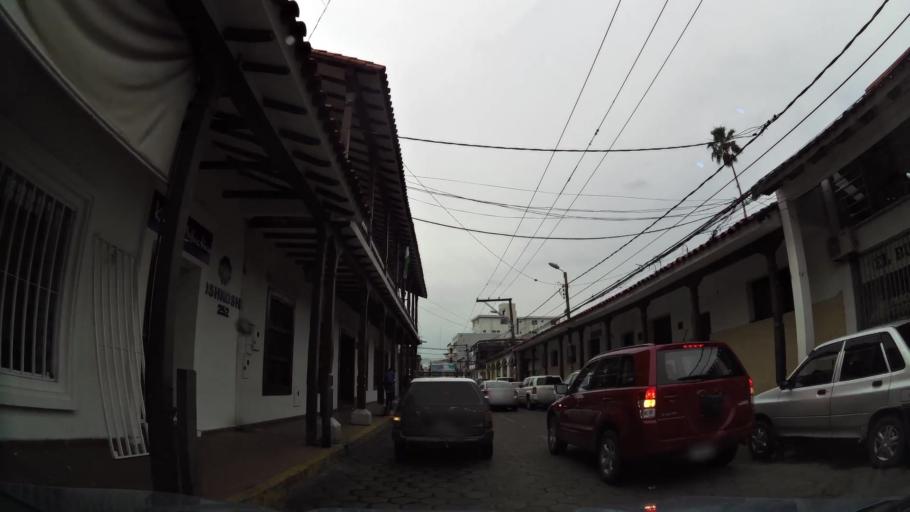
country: BO
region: Santa Cruz
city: Santa Cruz de la Sierra
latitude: -17.7864
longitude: -63.1824
